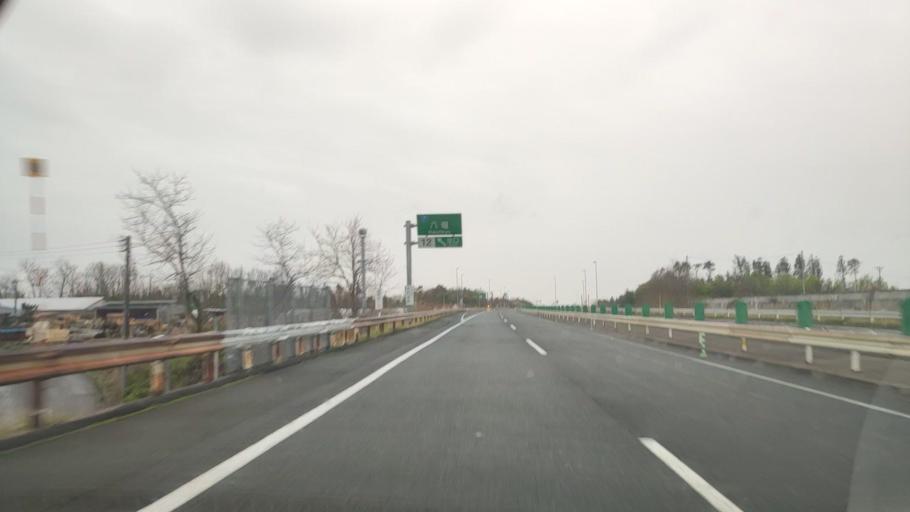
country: JP
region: Akita
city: Noshiromachi
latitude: 40.1225
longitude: 140.0121
